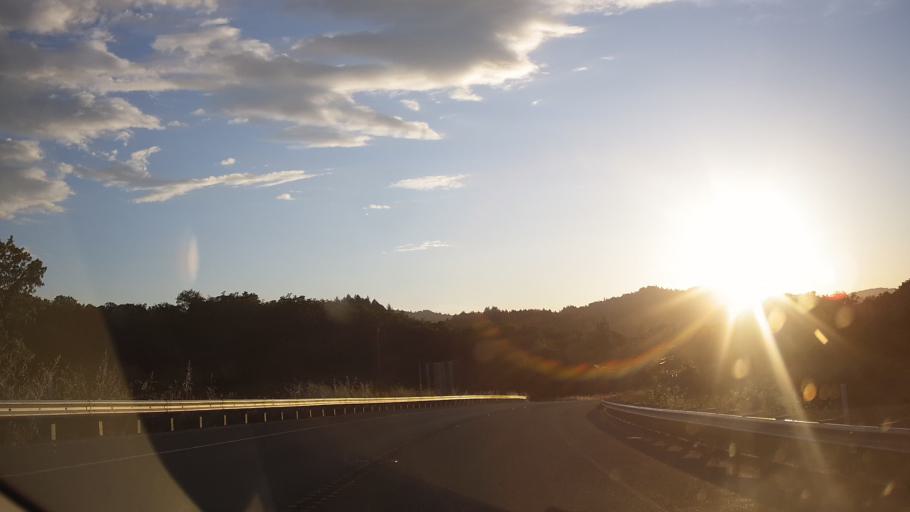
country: US
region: California
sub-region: Mendocino County
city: Willits
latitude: 39.3746
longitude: -123.3292
